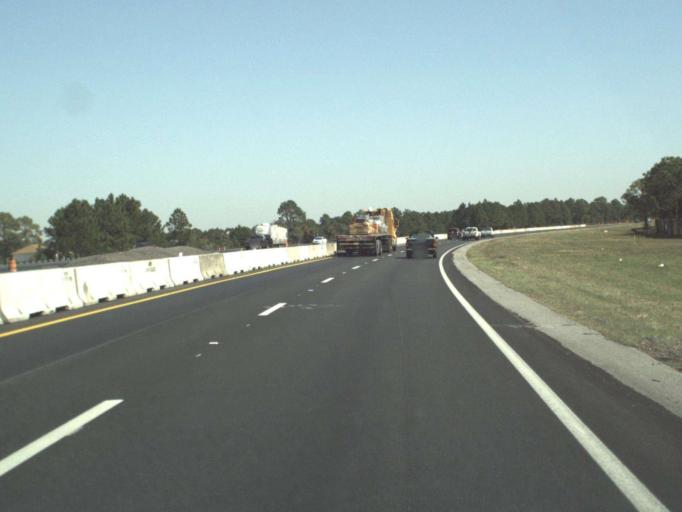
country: US
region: Florida
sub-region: Santa Rosa County
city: Pace
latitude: 30.5332
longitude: -87.1248
